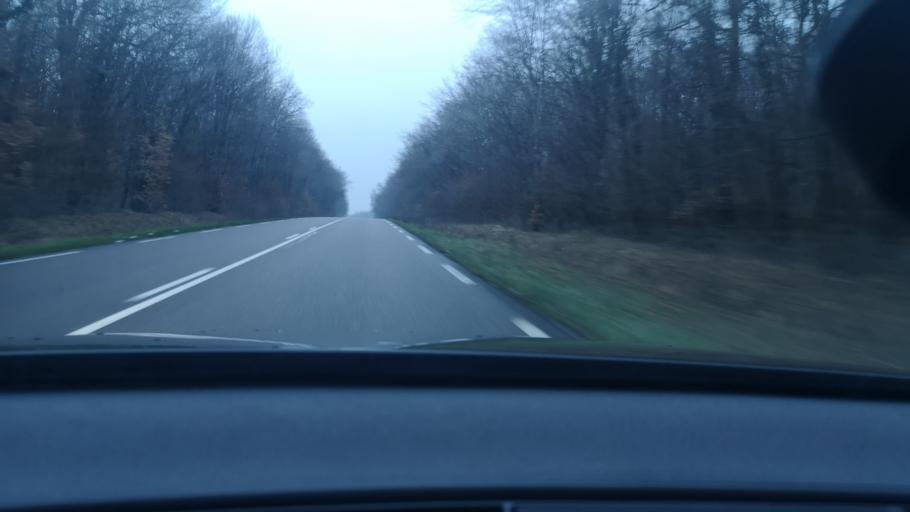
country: FR
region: Bourgogne
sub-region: Departement de la Cote-d'Or
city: Aiserey
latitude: 47.0975
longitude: 5.1035
